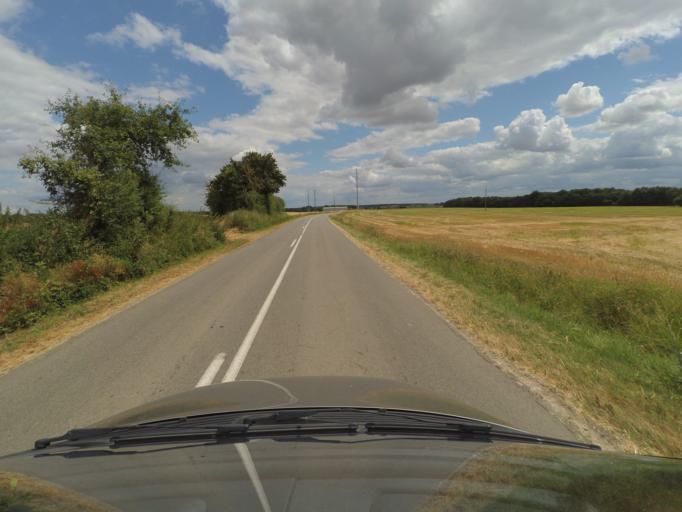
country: FR
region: Poitou-Charentes
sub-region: Departement de la Vienne
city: Saint-Savin
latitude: 46.5593
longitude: 0.9505
